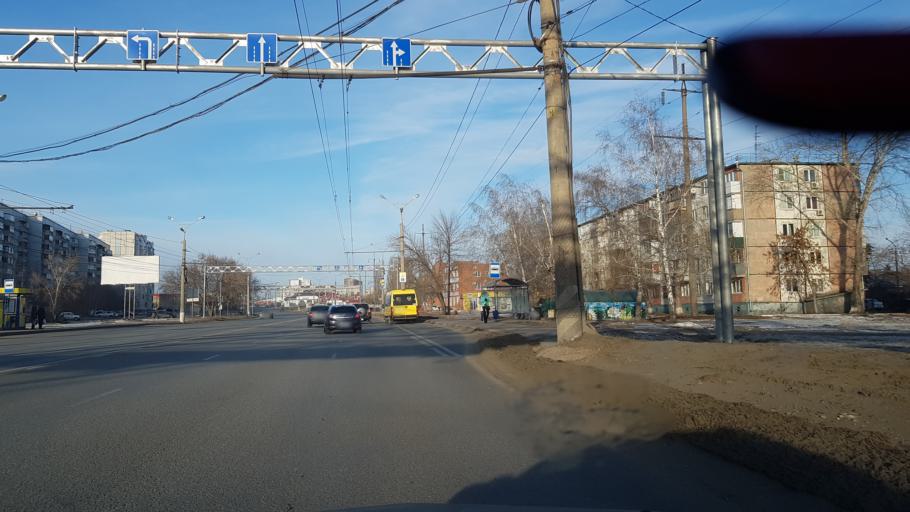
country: RU
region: Samara
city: Tol'yatti
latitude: 53.5301
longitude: 49.3966
